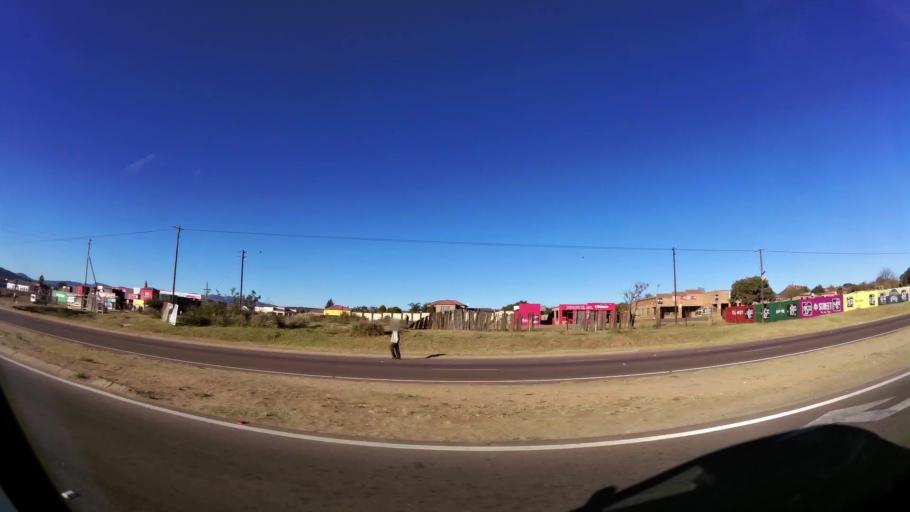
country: ZA
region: Limpopo
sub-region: Capricorn District Municipality
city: Mankoeng
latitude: -23.9106
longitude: 29.7762
